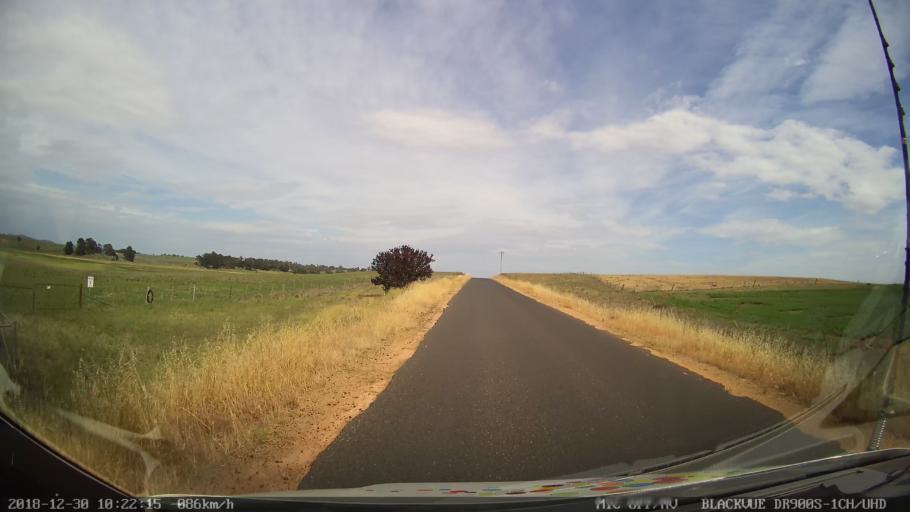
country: AU
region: New South Wales
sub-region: Snowy River
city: Berridale
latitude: -36.5452
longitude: 148.9976
